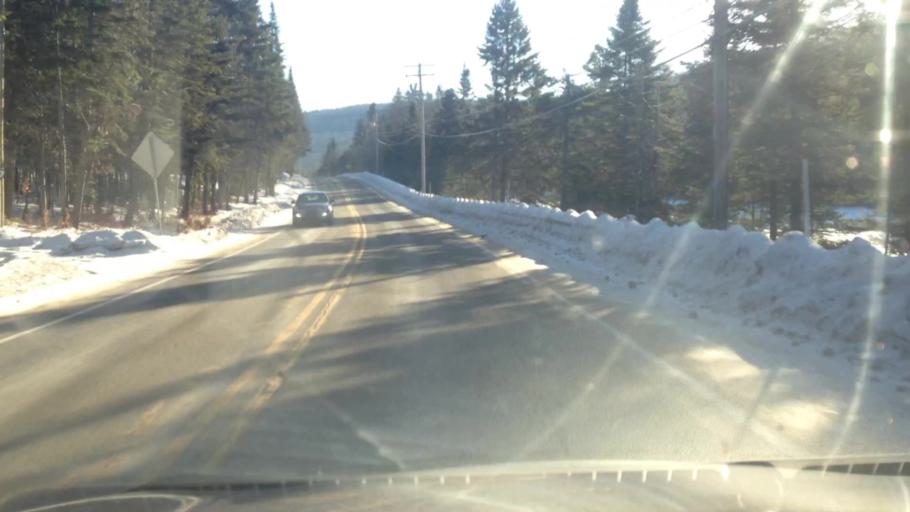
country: CA
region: Quebec
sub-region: Laurentides
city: Saint-Sauveur
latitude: 45.9065
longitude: -74.3248
